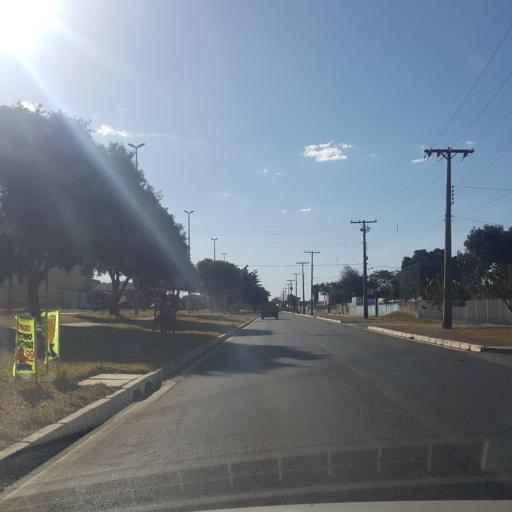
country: BR
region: Federal District
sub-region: Brasilia
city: Brasilia
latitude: -15.8022
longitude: -48.1065
